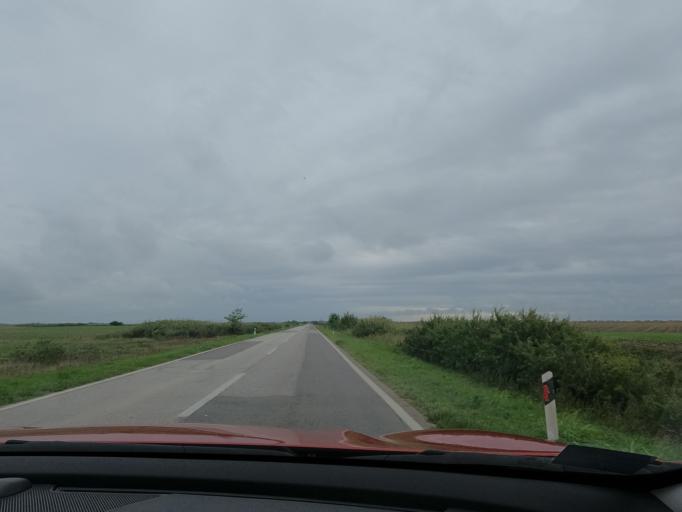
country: RS
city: Basaid
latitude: 45.6111
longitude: 20.3983
